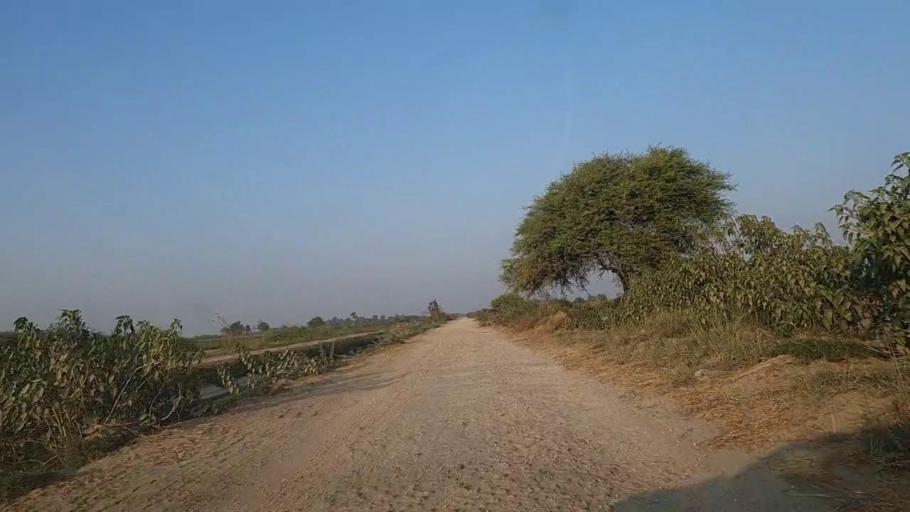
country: PK
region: Sindh
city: Keti Bandar
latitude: 24.2803
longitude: 67.6867
